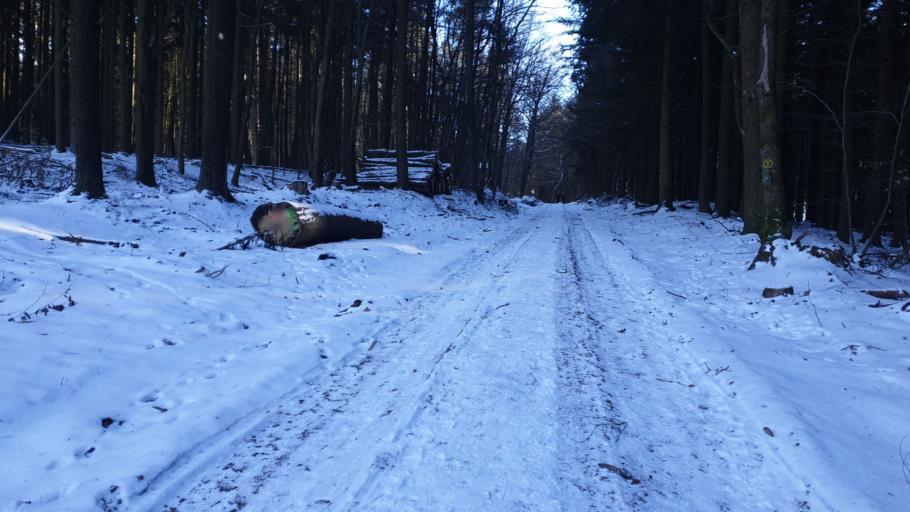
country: DE
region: Hesse
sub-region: Regierungsbezirk Darmstadt
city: Beerfelden
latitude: 49.5479
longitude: 8.9913
